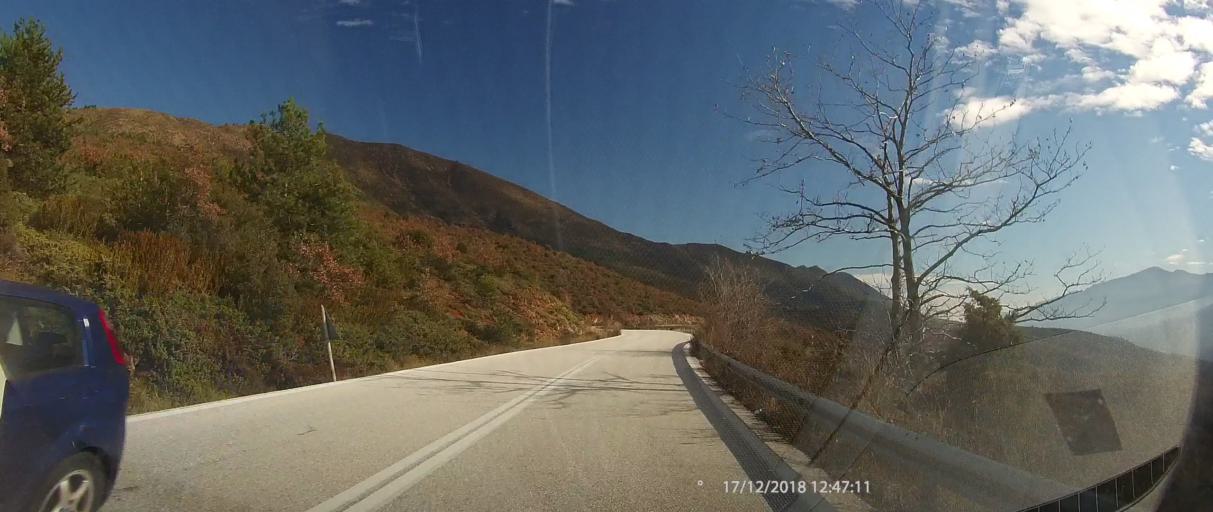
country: GR
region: Thessaly
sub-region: Trikala
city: Kastraki
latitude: 39.7856
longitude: 21.4245
